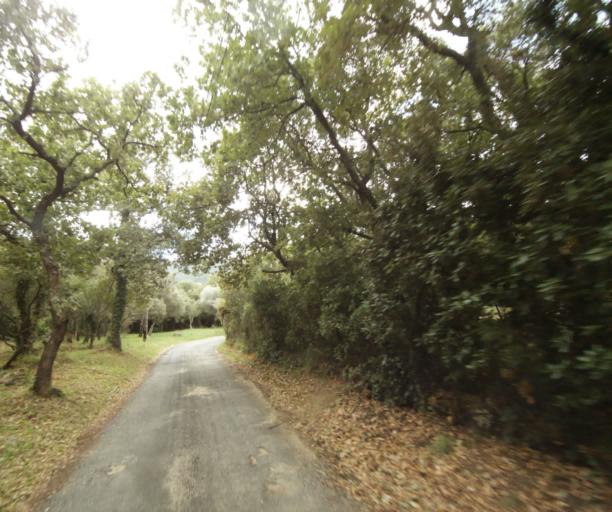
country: FR
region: Languedoc-Roussillon
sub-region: Departement des Pyrenees-Orientales
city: Argelers
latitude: 42.5377
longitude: 3.0010
